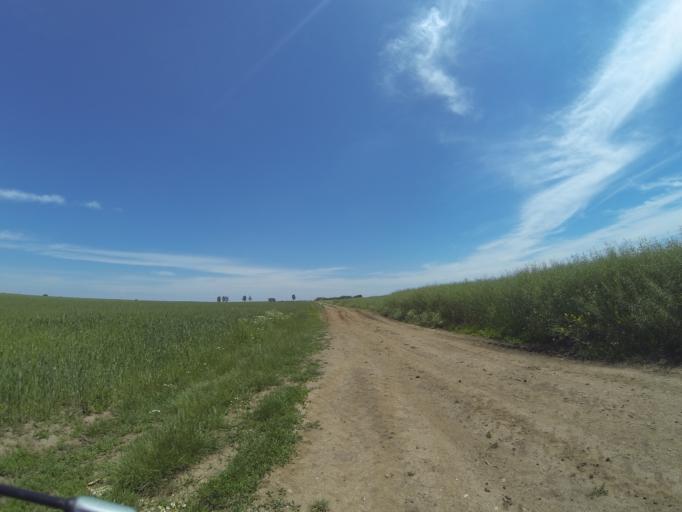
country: RO
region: Dolj
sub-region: Comuna Diosti
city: Radomir
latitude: 44.1468
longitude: 24.1545
